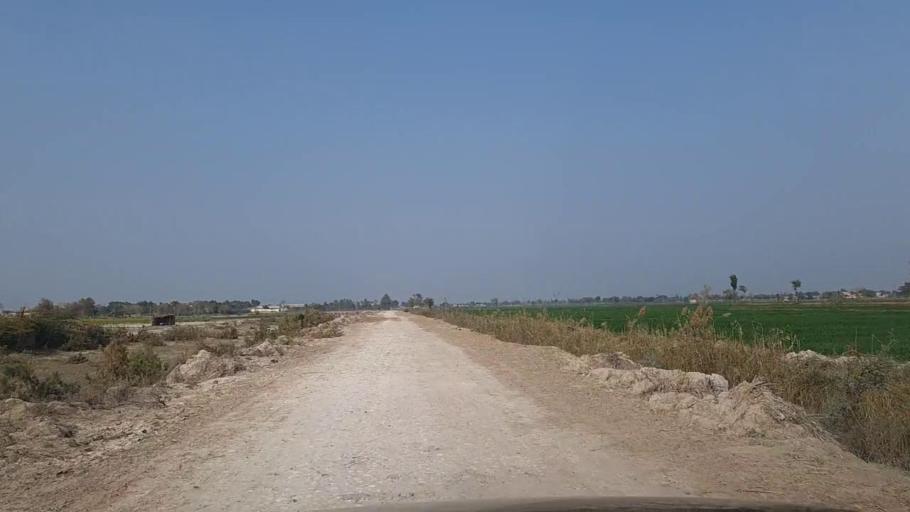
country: PK
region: Sindh
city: Daur
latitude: 26.3878
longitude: 68.4236
